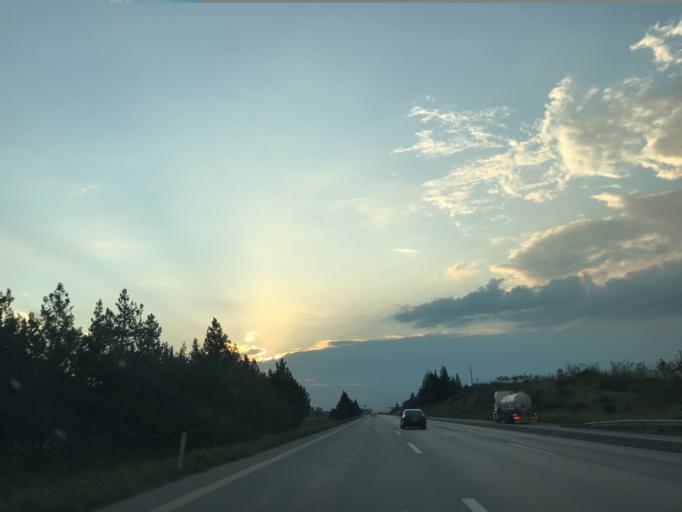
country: TR
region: Mersin
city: Yenice
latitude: 37.0235
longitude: 35.0544
